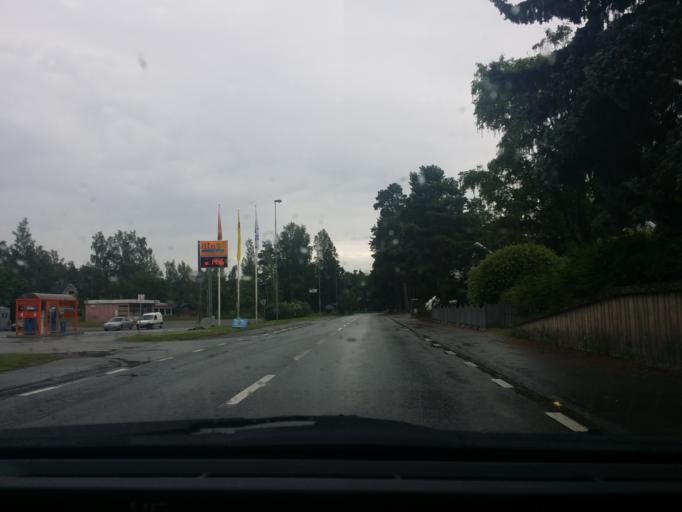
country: SE
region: OErebro
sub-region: Lindesbergs Kommun
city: Fellingsbro
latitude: 59.4311
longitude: 15.5952
